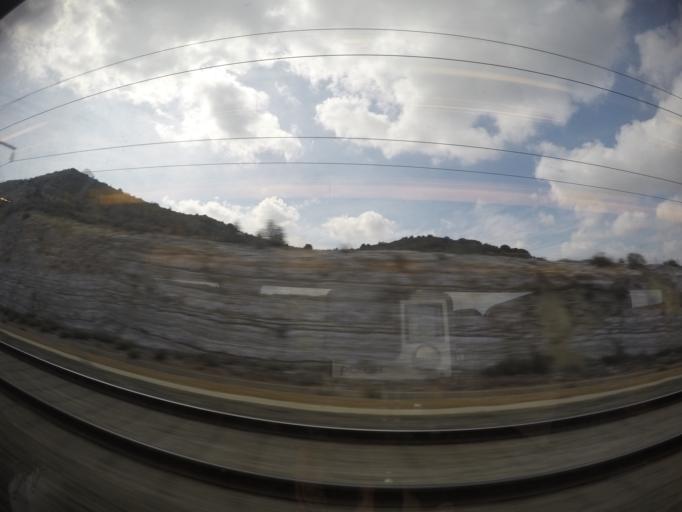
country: ES
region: Aragon
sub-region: Provincia de Huesca
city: Castejon de Monegros
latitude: 41.5309
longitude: -0.3267
